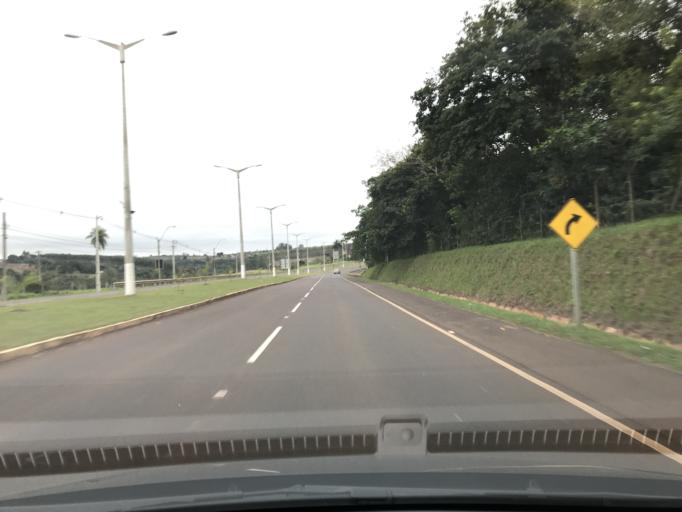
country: PY
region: Canindeyu
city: Salto del Guaira
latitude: -24.0227
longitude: -54.3249
